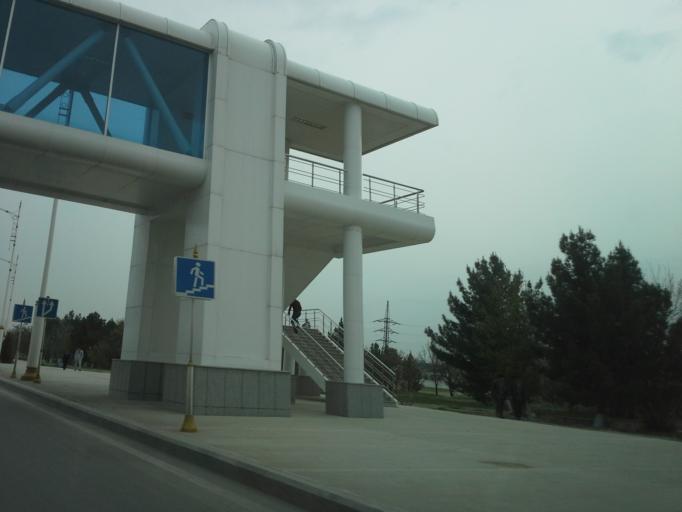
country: TM
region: Ahal
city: Ashgabat
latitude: 37.9654
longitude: 58.3586
